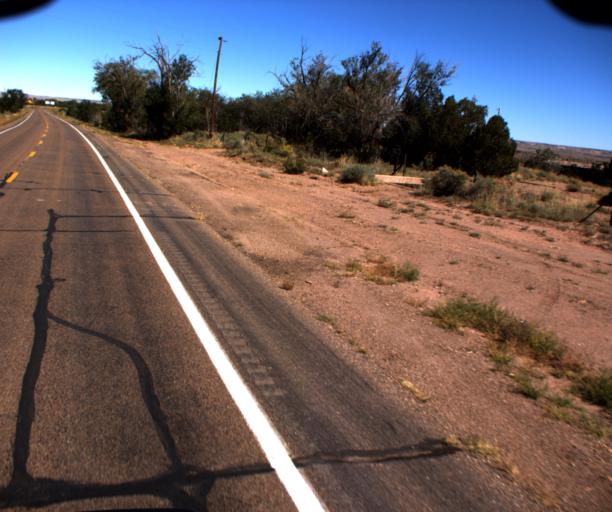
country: US
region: Arizona
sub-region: Apache County
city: Saint Johns
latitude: 34.4792
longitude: -109.3855
